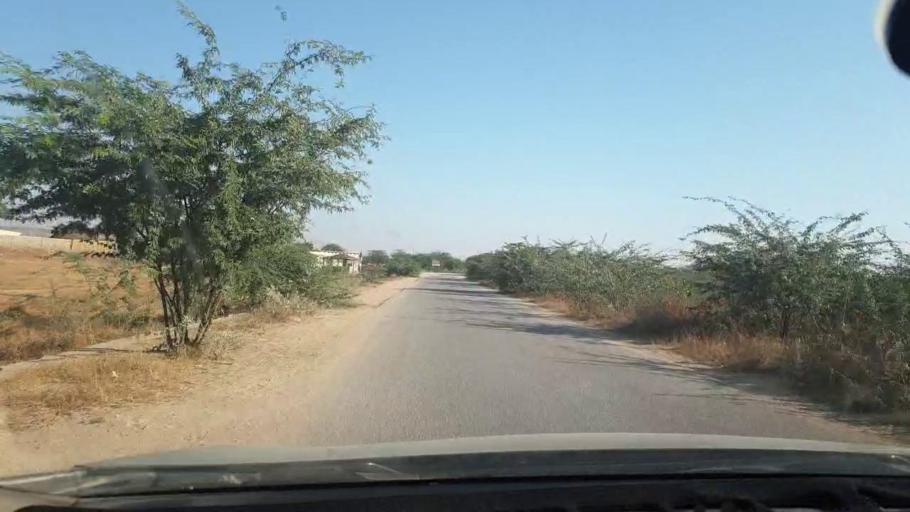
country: PK
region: Sindh
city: Malir Cantonment
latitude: 25.1747
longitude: 67.2029
